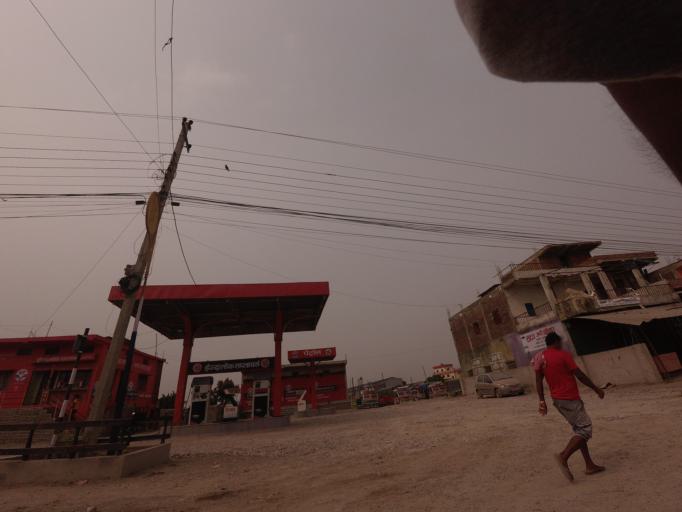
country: NP
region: Western Region
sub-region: Lumbini Zone
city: Bhairahawa
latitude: 27.5035
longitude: 83.3751
